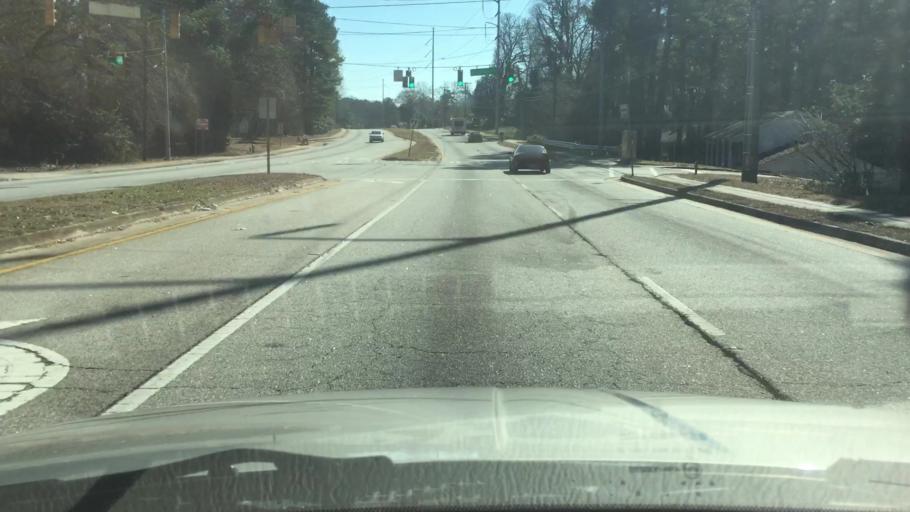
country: US
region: Georgia
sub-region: DeKalb County
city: Redan
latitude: 33.7483
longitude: -84.1971
